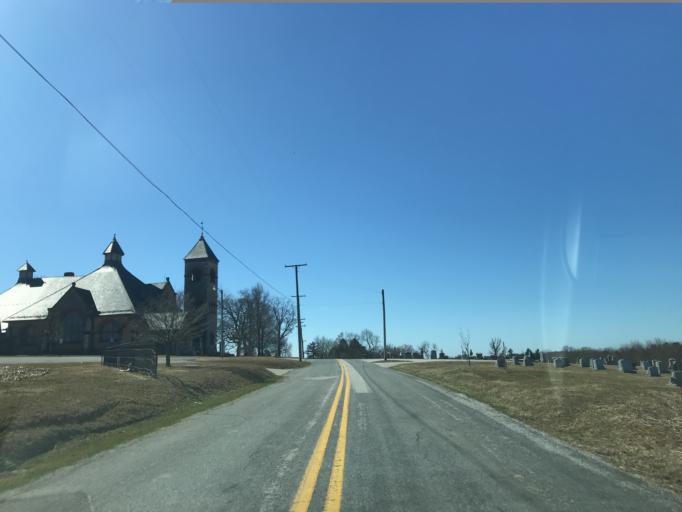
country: US
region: Pennsylvania
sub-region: York County
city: Stewartstown
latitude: 39.7246
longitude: -76.5221
